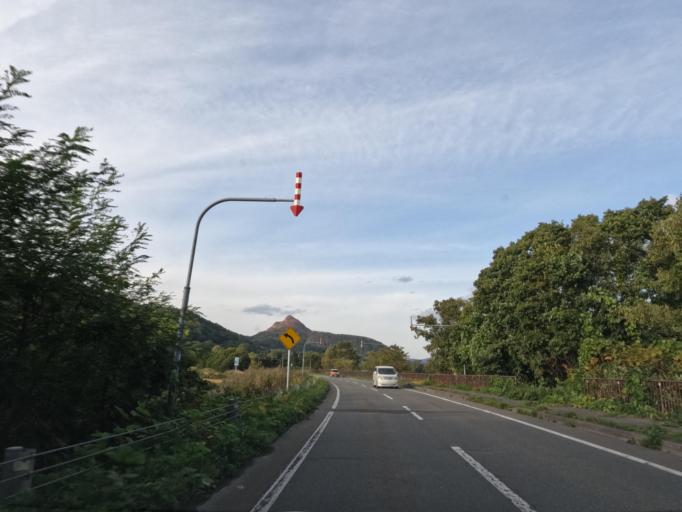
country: JP
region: Hokkaido
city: Date
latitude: 42.5143
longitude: 140.8641
